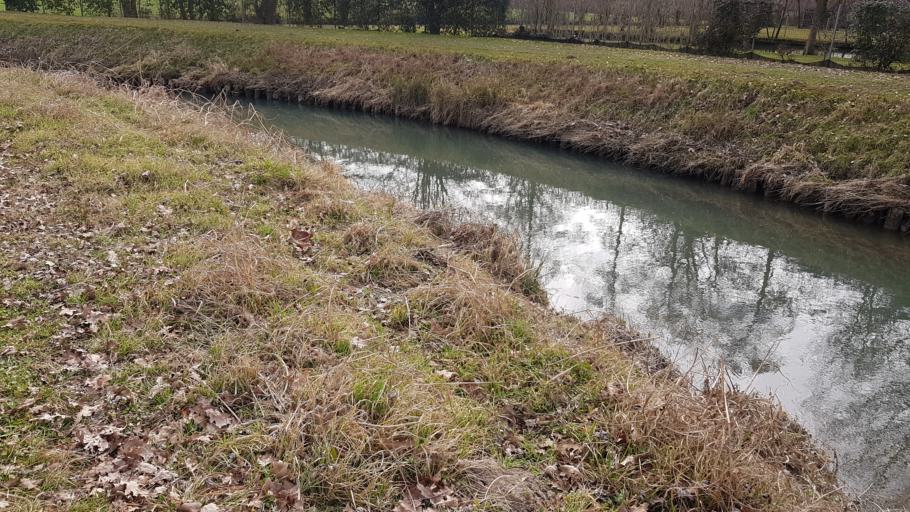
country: IT
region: Veneto
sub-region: Provincia di Padova
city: San Giorgio delle Pertiche
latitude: 45.5463
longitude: 11.9075
